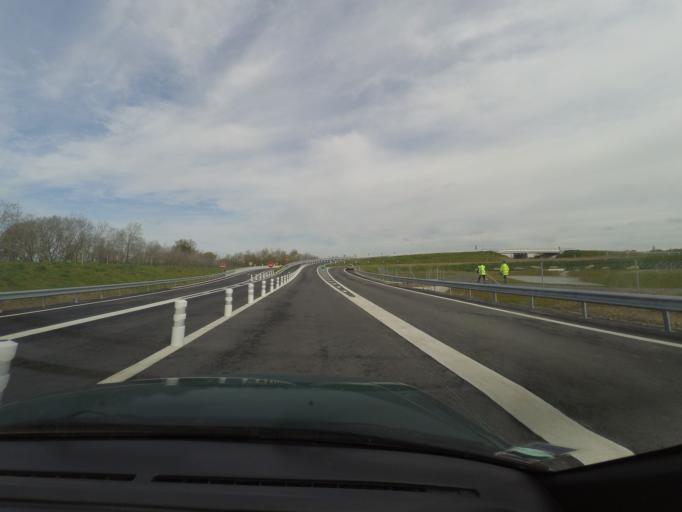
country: FR
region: Pays de la Loire
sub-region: Departement de la Loire-Atlantique
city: Aigrefeuille-sur-Maine
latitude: 47.0707
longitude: -1.4383
